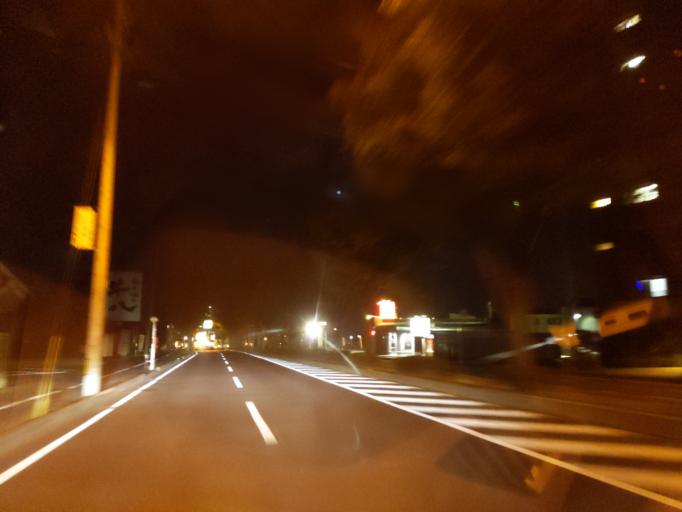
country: JP
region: Okayama
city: Okayama-shi
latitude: 34.6802
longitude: 133.9422
